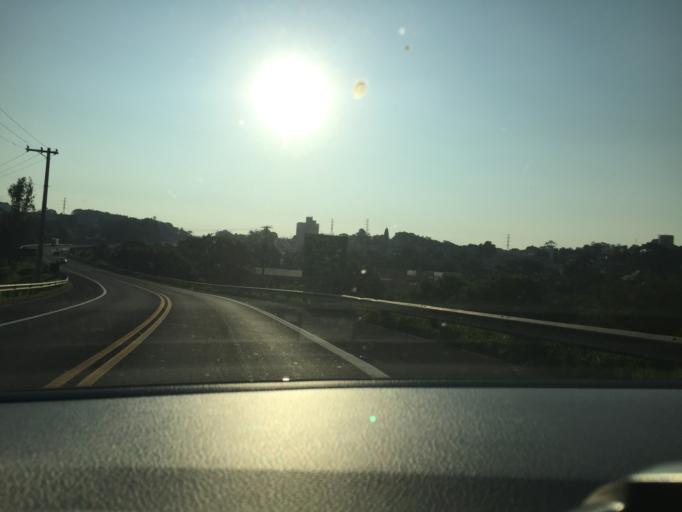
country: BR
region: Sao Paulo
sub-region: Louveira
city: Louveira
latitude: -23.0881
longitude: -46.9459
